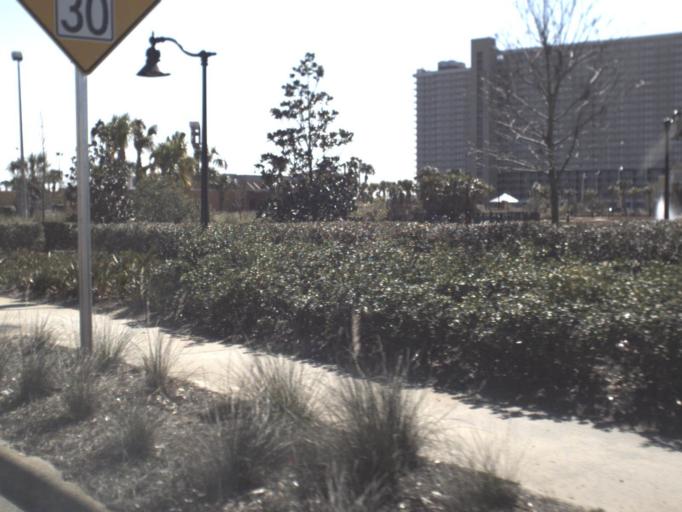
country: US
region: Florida
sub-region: Bay County
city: Panama City Beach
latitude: 30.1797
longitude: -85.8022
